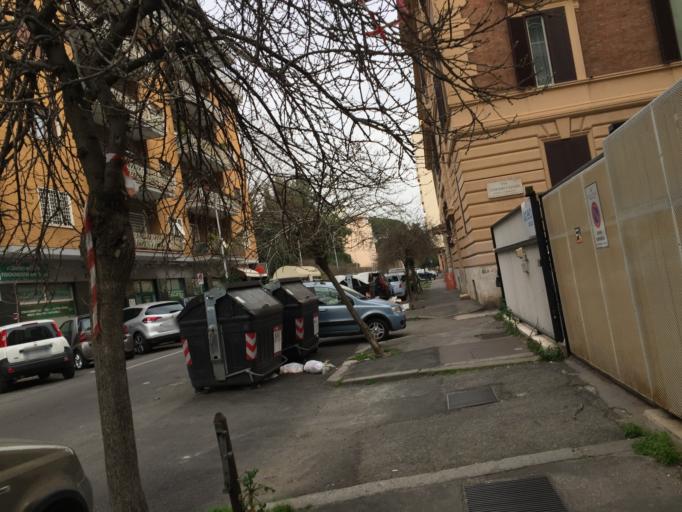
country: VA
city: Vatican City
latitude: 41.8826
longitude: 12.4610
